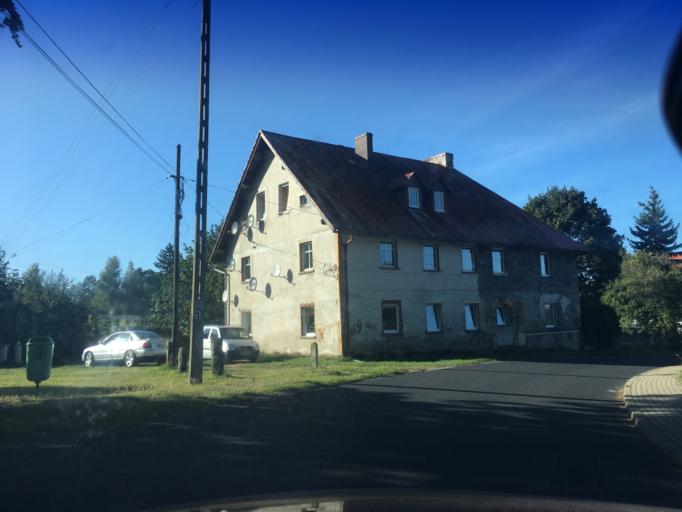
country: PL
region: Lower Silesian Voivodeship
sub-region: Powiat lubanski
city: Swieradow-Zdroj
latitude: 50.9299
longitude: 15.3040
